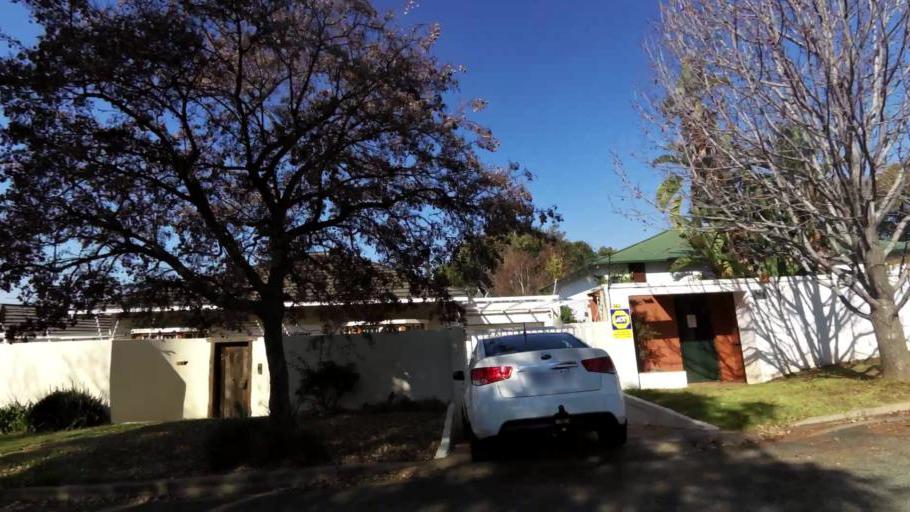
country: ZA
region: Gauteng
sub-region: City of Johannesburg Metropolitan Municipality
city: Johannesburg
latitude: -26.1766
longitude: 27.9897
